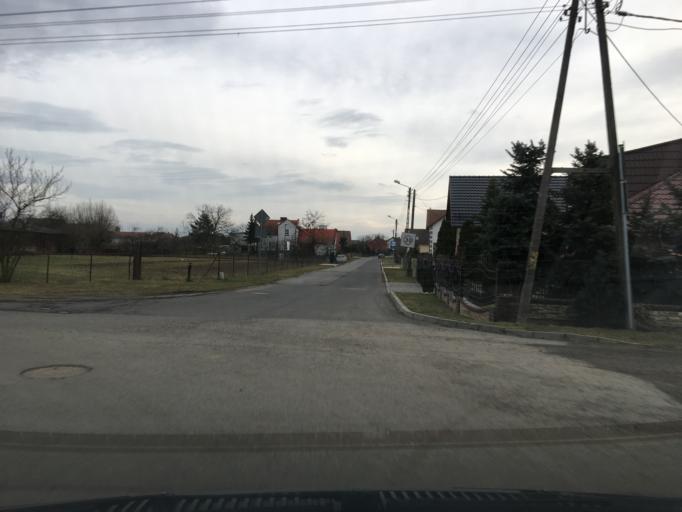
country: PL
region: Opole Voivodeship
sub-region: Powiat kedzierzynsko-kozielski
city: Wiekszyce
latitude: 50.3565
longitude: 18.1185
